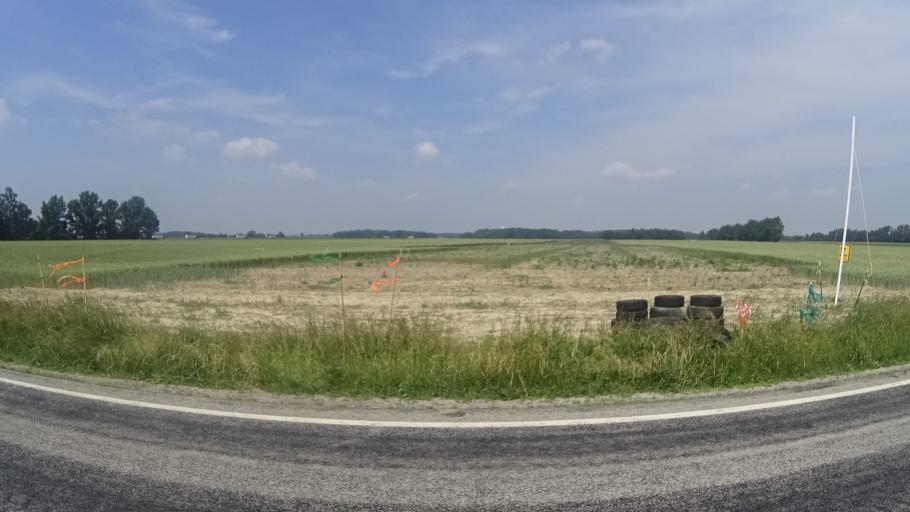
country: US
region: Ohio
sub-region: Huron County
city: Monroeville
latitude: 41.3408
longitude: -82.7233
